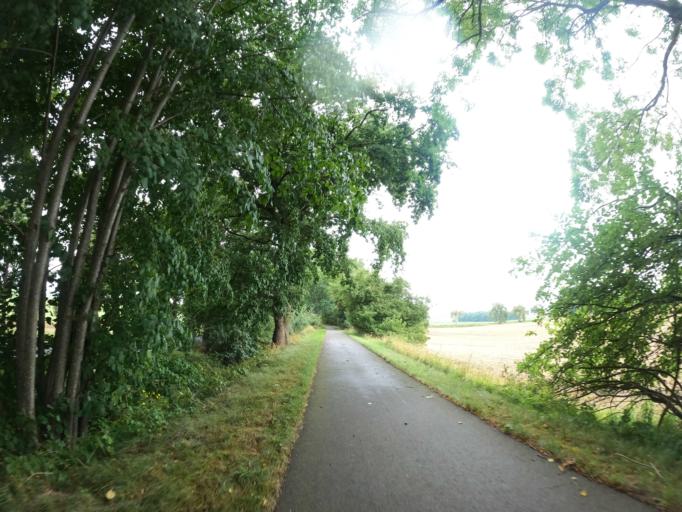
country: DE
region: Mecklenburg-Vorpommern
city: Poseritz
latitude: 54.2942
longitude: 13.3002
